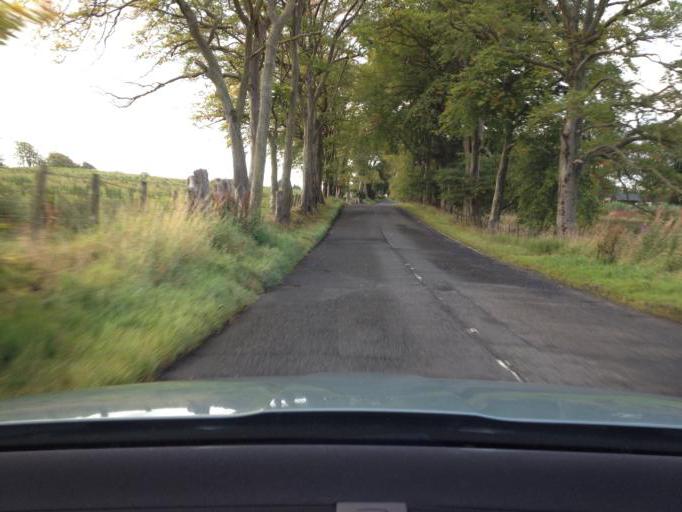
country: GB
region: Scotland
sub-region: West Lothian
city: West Calder
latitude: 55.8351
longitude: -3.5352
